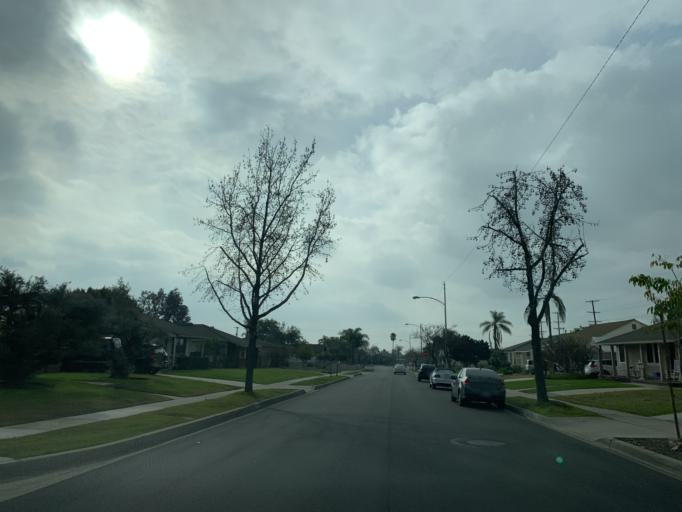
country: US
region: California
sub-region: Los Angeles County
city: Azusa
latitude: 34.1291
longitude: -117.9158
